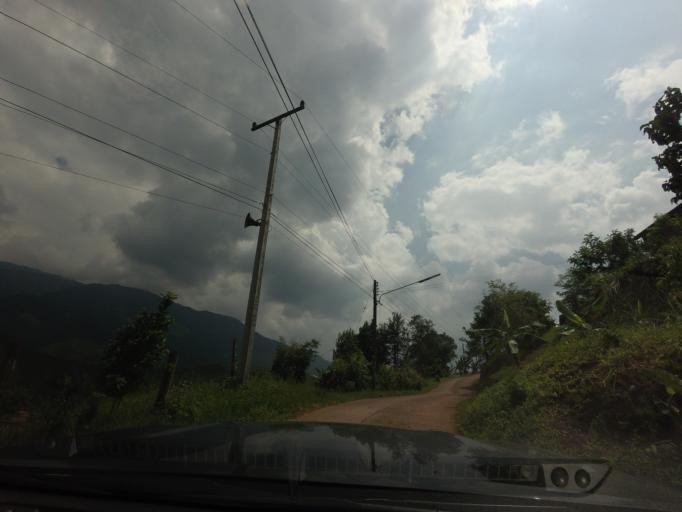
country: TH
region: Nan
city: Bo Kluea
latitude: 19.1903
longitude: 101.2004
